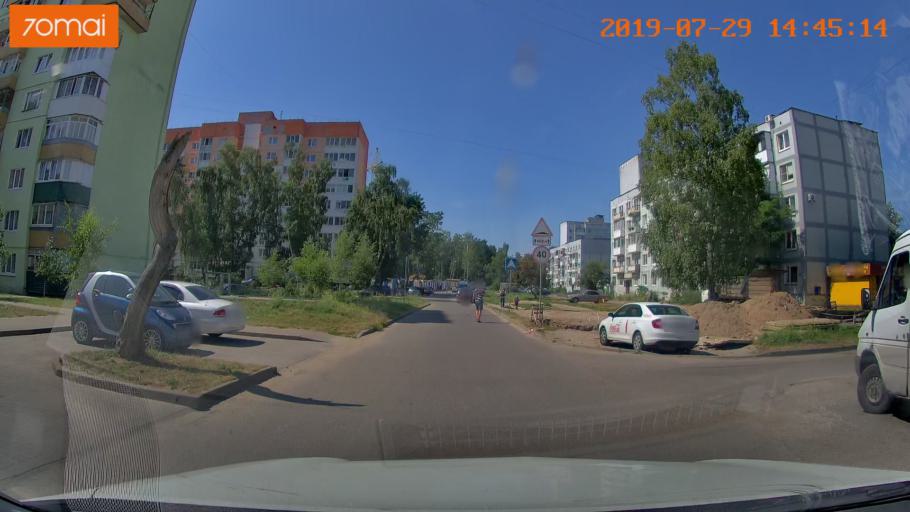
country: RU
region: Kaliningrad
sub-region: Gorod Kaliningrad
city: Baltiysk
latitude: 54.6635
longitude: 19.9060
